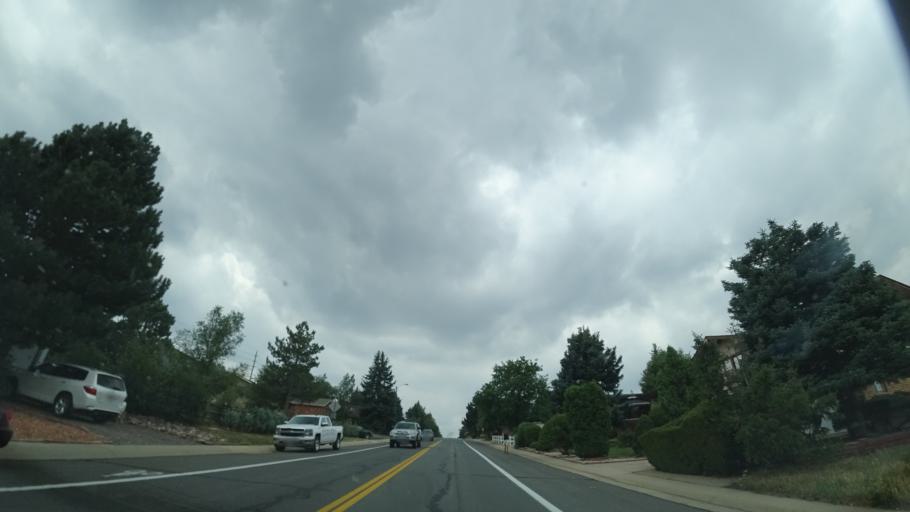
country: US
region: Colorado
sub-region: Jefferson County
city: West Pleasant View
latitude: 39.7103
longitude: -105.1478
